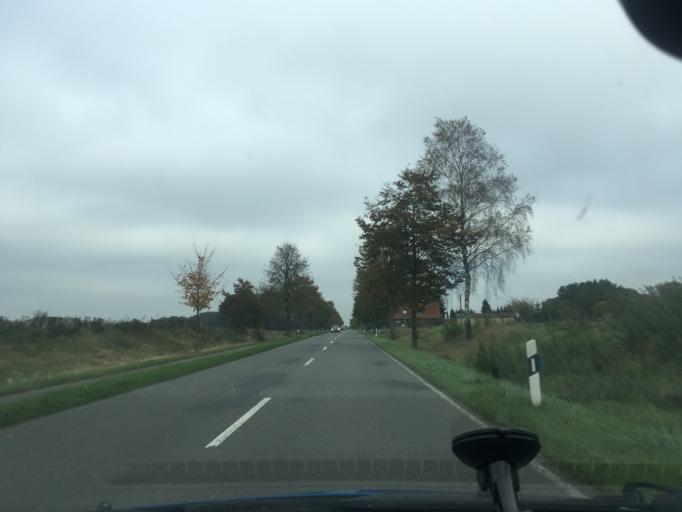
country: DE
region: Lower Saxony
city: Bispingen
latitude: 53.0774
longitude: 9.9817
